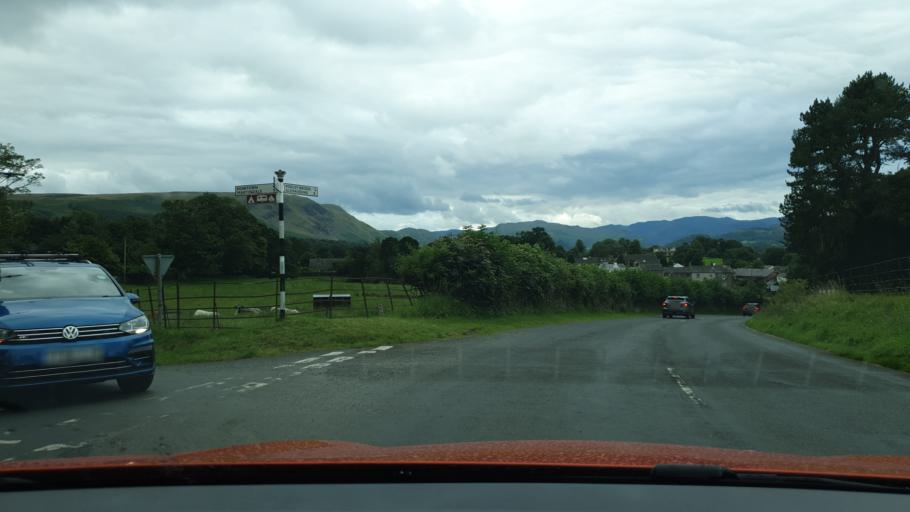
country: GB
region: England
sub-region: Cumbria
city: Penrith
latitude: 54.6139
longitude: -2.8136
